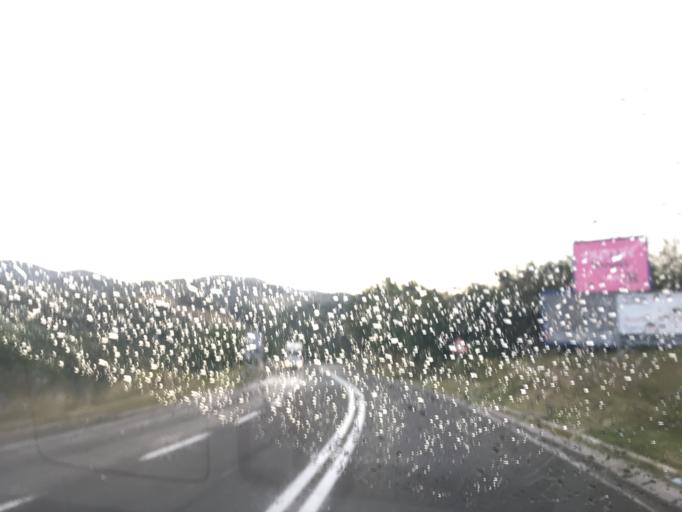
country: RS
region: Central Serbia
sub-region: Moravicki Okrug
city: Gornji Milanovac
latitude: 44.1181
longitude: 20.4828
